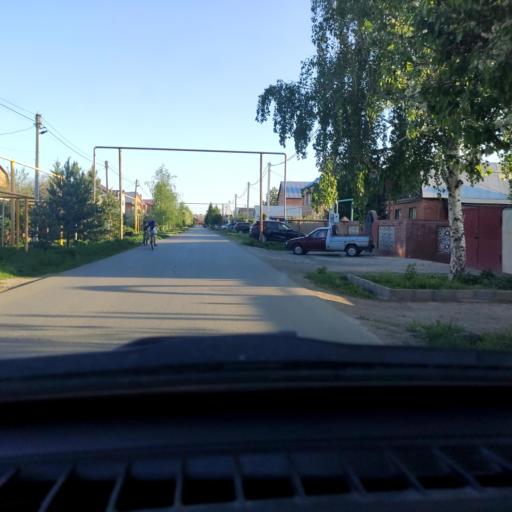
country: RU
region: Samara
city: Tol'yatti
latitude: 53.5600
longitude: 49.4021
